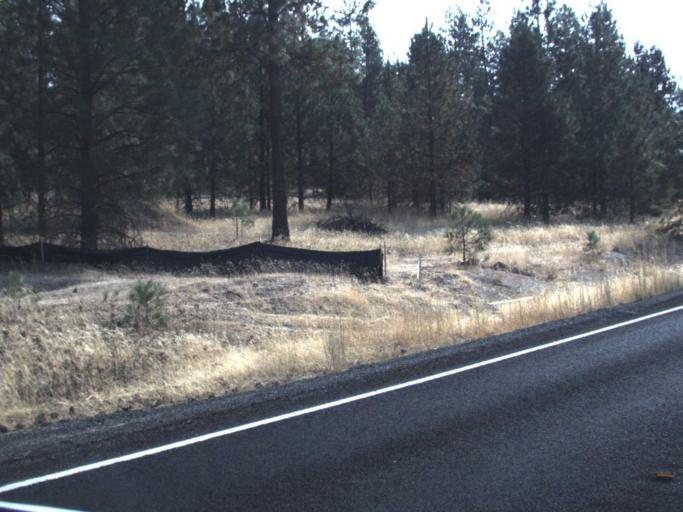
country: US
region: Washington
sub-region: Spokane County
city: Deer Park
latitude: 47.8244
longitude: -117.5920
